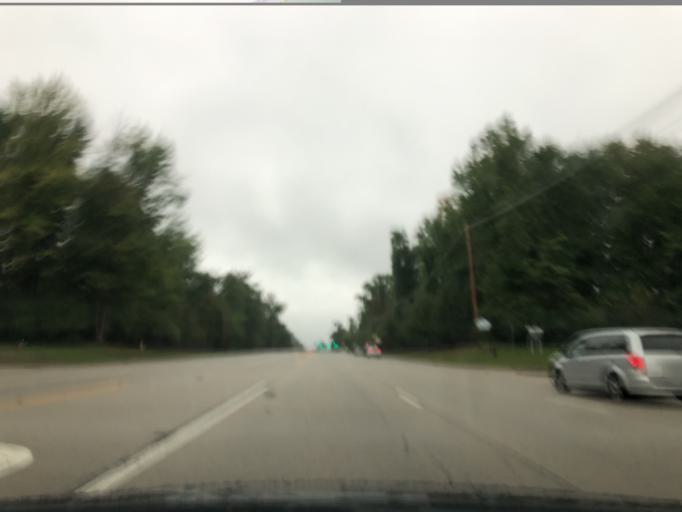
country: US
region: Ohio
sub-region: Hamilton County
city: Highpoint
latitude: 39.2801
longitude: -84.3727
